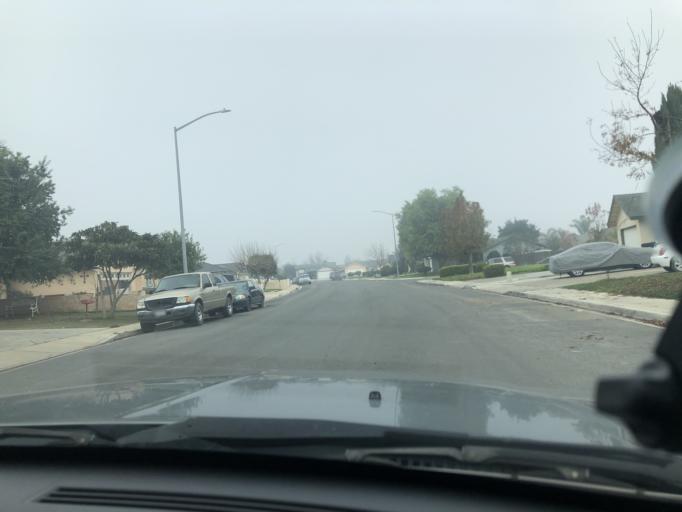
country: US
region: California
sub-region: Monterey County
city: King City
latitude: 36.2073
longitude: -121.1435
